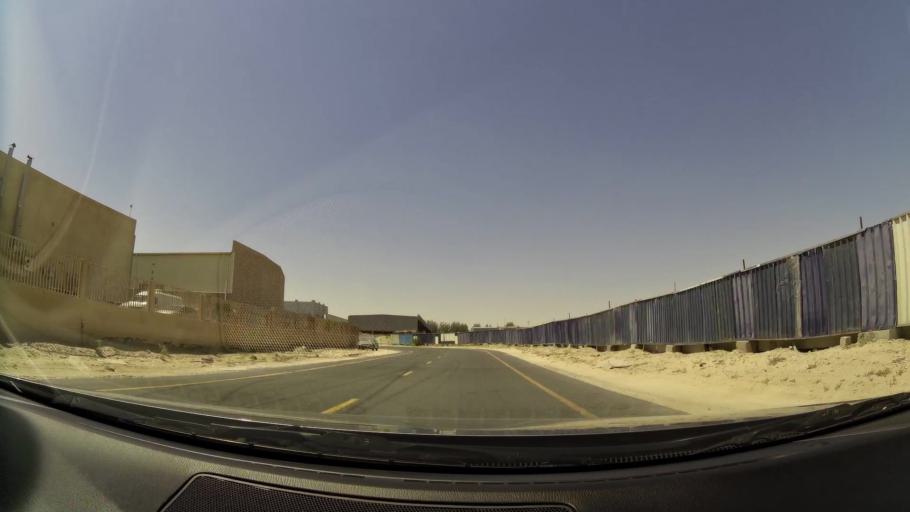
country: AE
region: Dubai
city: Dubai
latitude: 24.9750
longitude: 55.1862
